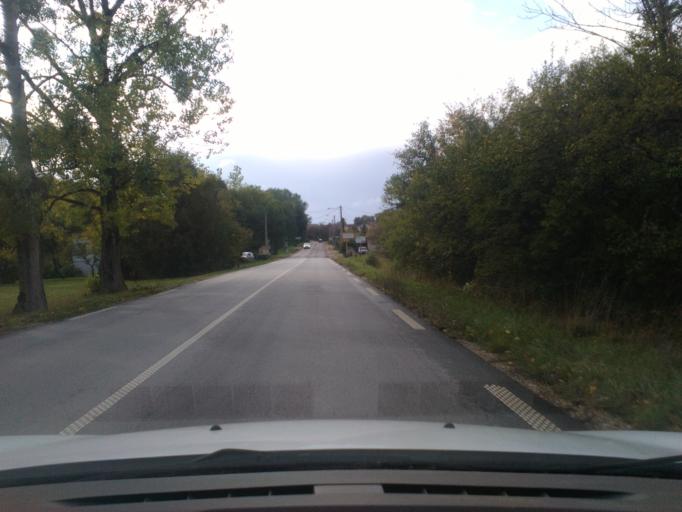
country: FR
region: Lorraine
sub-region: Departement des Vosges
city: Aydoilles
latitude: 48.2479
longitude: 6.6096
